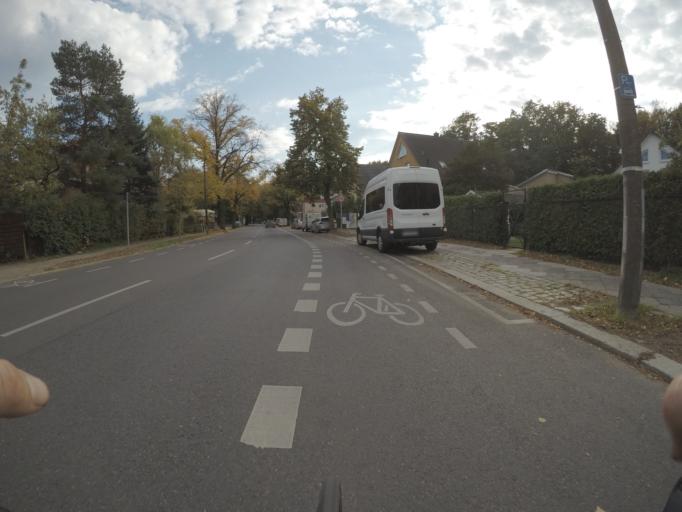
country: DE
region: Berlin
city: Wilhelmsruh
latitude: 52.5825
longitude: 13.3747
